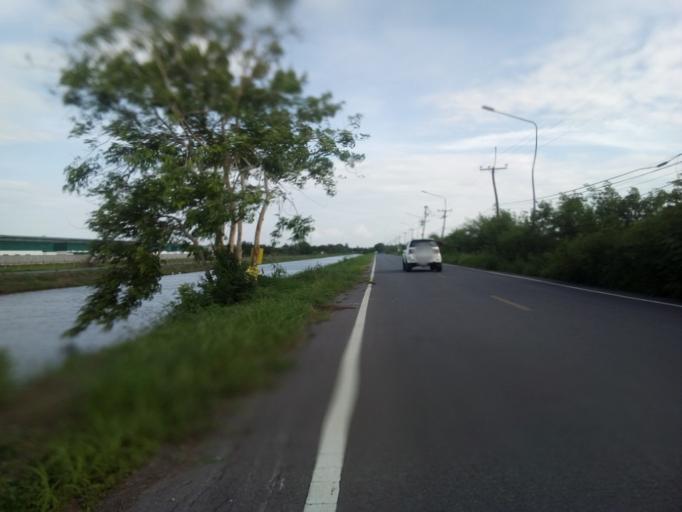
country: TH
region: Pathum Thani
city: Nong Suea
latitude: 14.0692
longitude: 100.8464
